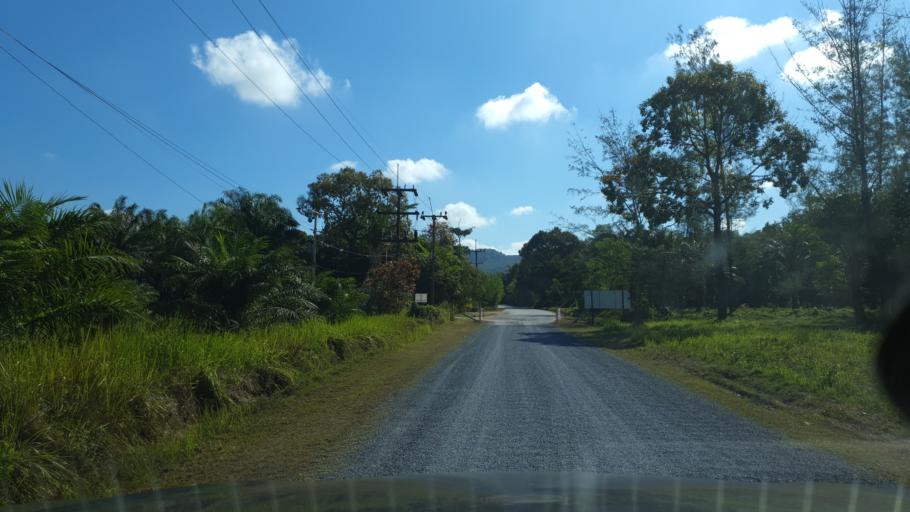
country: TH
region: Phangnga
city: Ban Ao Nang
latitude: 8.0496
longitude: 98.8011
